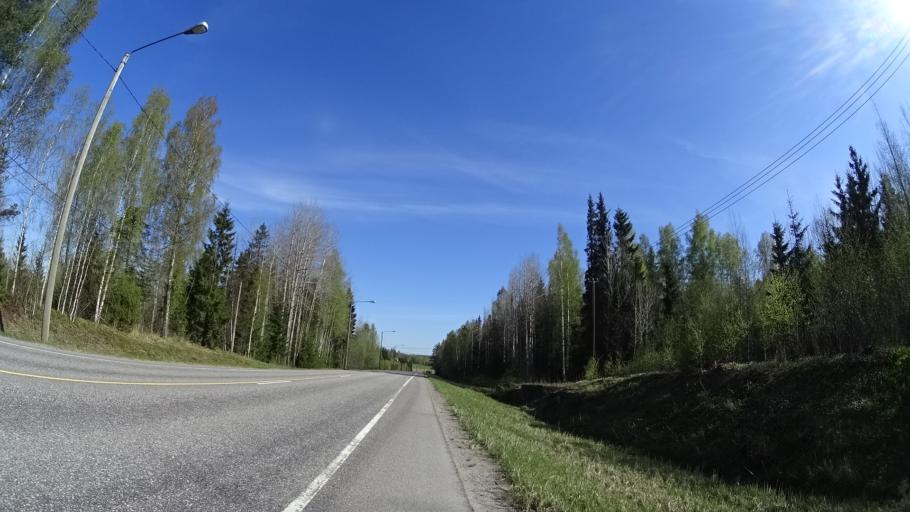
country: FI
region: Uusimaa
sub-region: Helsinki
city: Nurmijaervi
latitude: 60.3849
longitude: 24.8078
